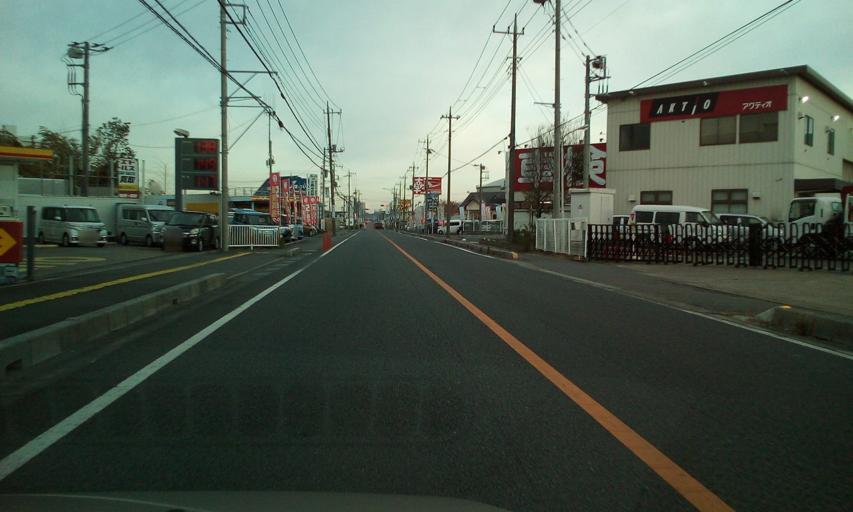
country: JP
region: Saitama
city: Yashio-shi
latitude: 35.8488
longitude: 139.8646
